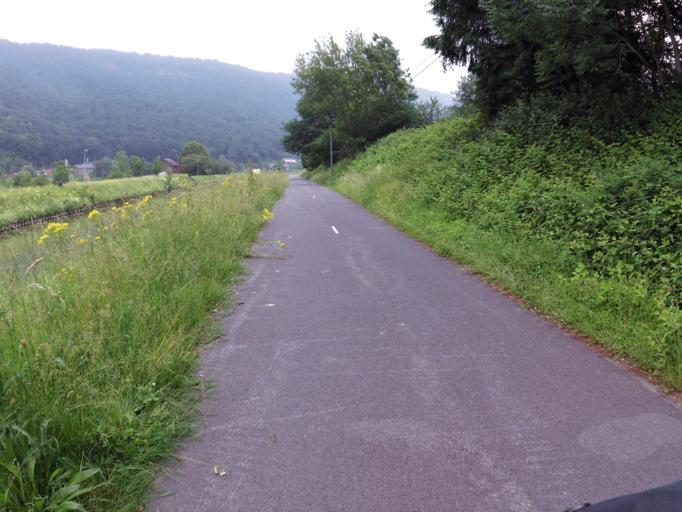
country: FR
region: Champagne-Ardenne
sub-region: Departement des Ardennes
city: Haybes
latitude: 50.0043
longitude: 4.6957
